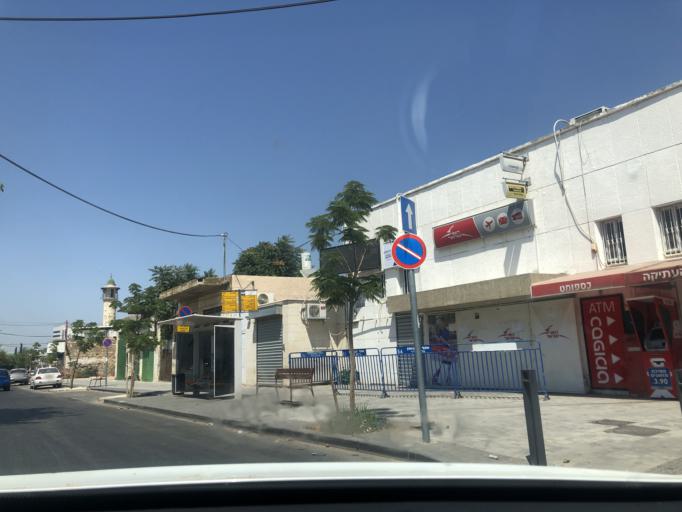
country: IL
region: Central District
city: Lod
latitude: 31.9555
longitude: 34.8962
